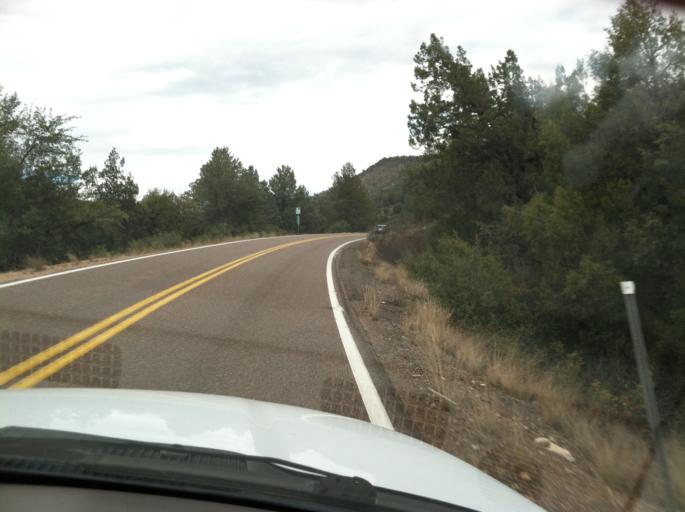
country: US
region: Arizona
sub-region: Gila County
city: Payson
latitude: 34.3118
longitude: -111.3672
